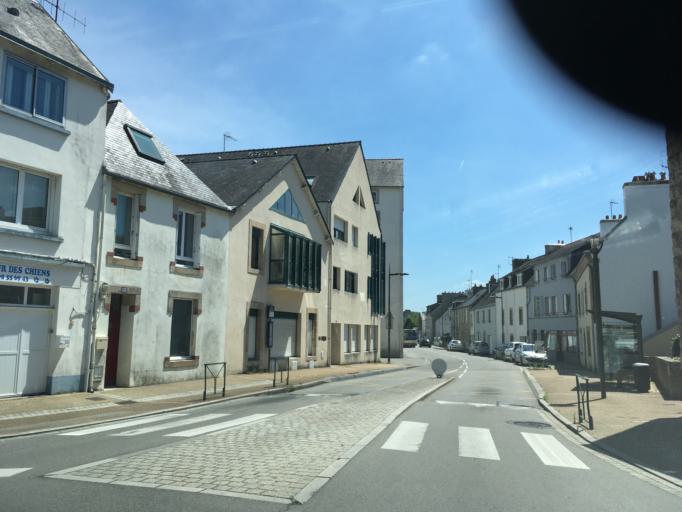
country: FR
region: Brittany
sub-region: Departement du Finistere
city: Quimper
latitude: 48.0042
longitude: -4.1173
